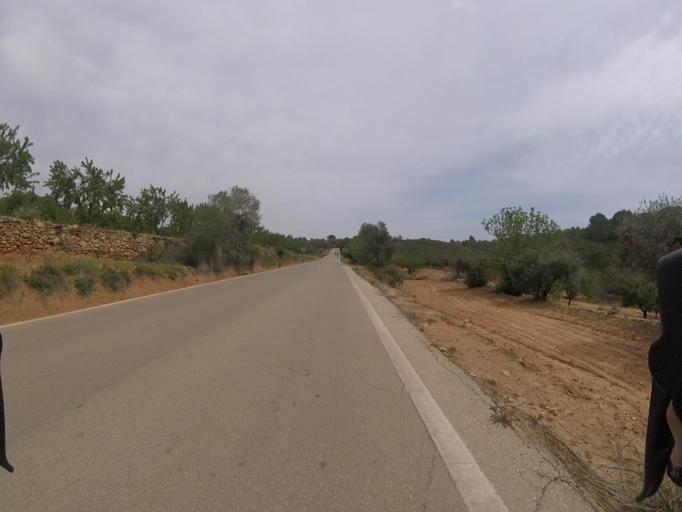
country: ES
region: Valencia
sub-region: Provincia de Castello
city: Cabanes
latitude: 40.1550
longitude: 0.0585
